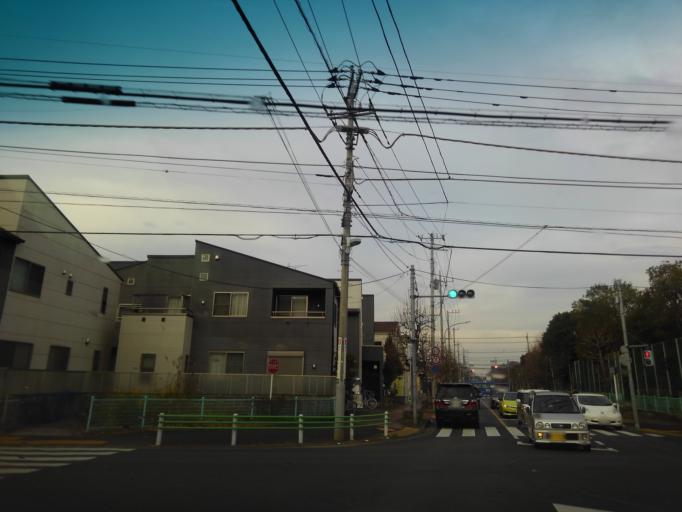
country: JP
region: Tokyo
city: Higashimurayama-shi
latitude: 35.7308
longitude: 139.4441
